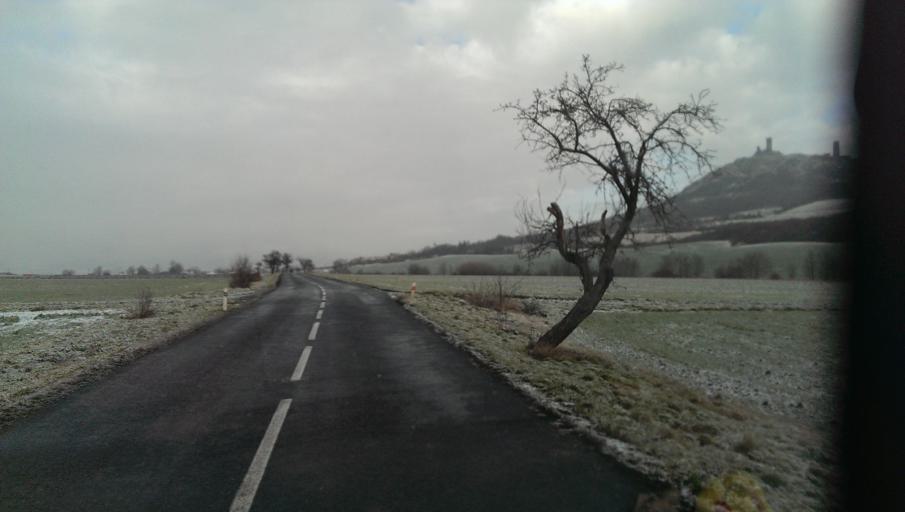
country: CZ
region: Ustecky
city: Libochovice
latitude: 50.4222
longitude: 14.0155
